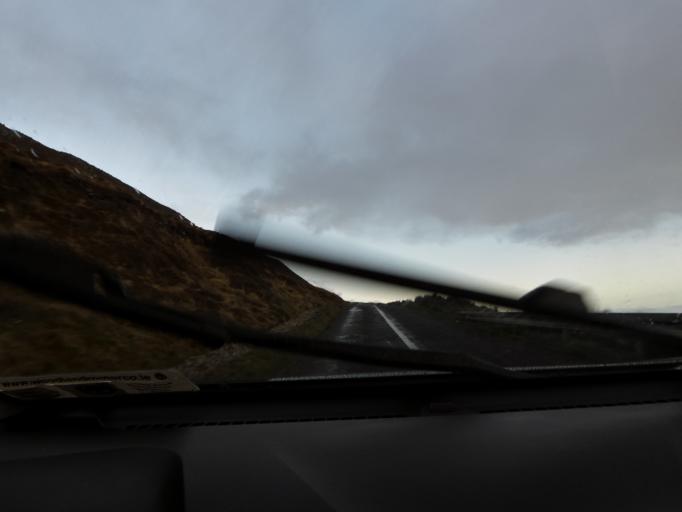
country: IE
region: Connaught
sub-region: Maigh Eo
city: Belmullet
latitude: 53.9704
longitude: -10.1830
